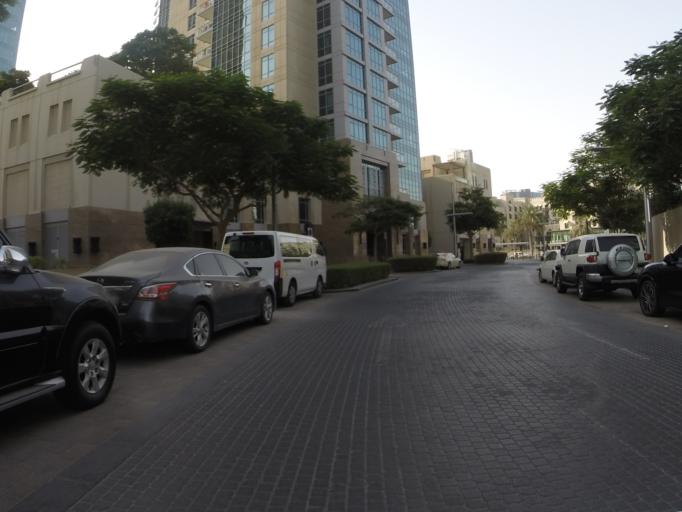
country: AE
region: Dubai
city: Dubai
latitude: 25.1918
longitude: 55.2739
